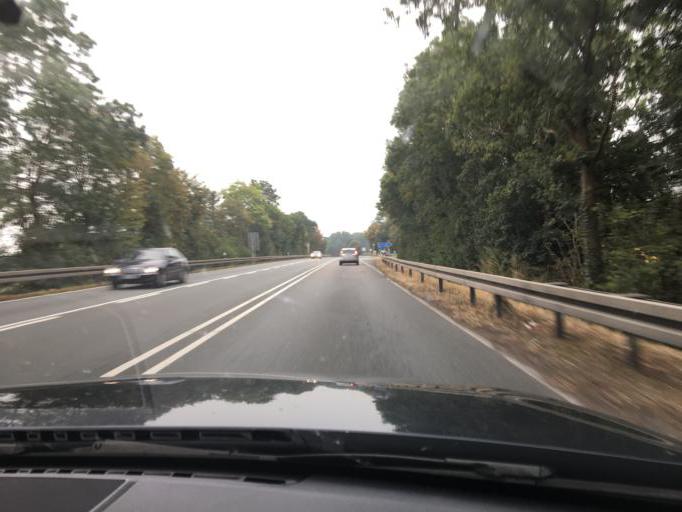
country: DE
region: North Rhine-Westphalia
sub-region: Regierungsbezirk Munster
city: Greven
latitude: 52.0859
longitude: 7.6418
